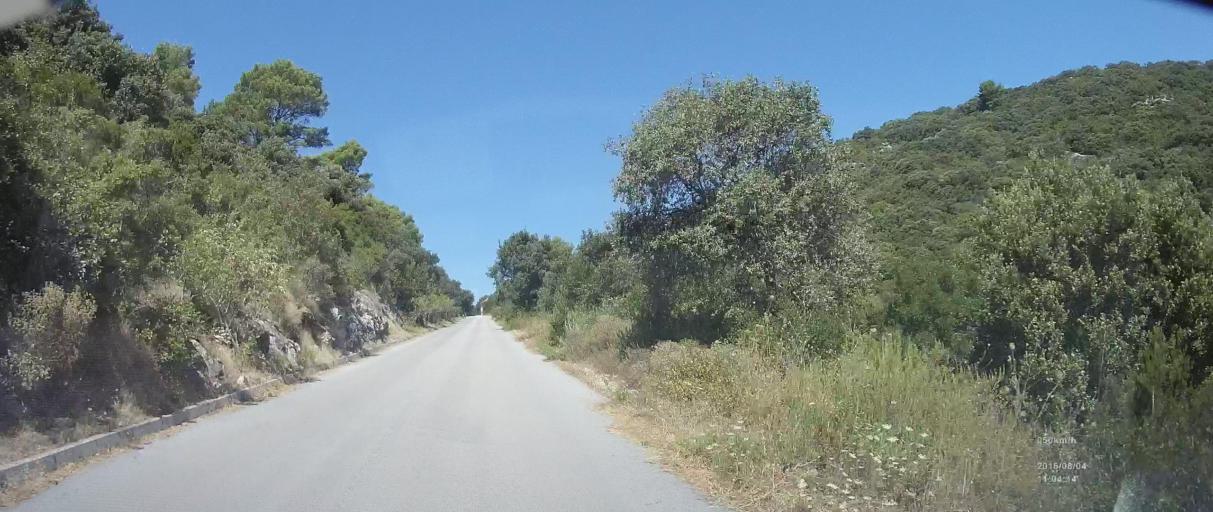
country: HR
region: Dubrovacko-Neretvanska
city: Blato
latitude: 42.7770
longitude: 17.4554
